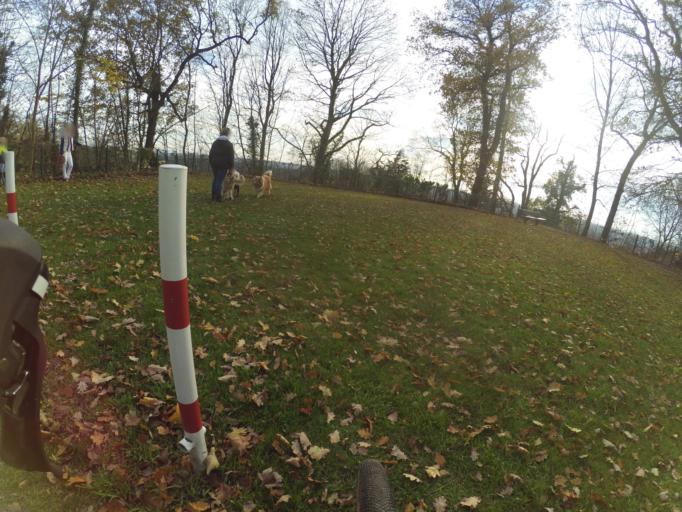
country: DE
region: North Rhine-Westphalia
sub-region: Regierungsbezirk Munster
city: Tecklenburg
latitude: 52.2187
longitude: 7.8096
